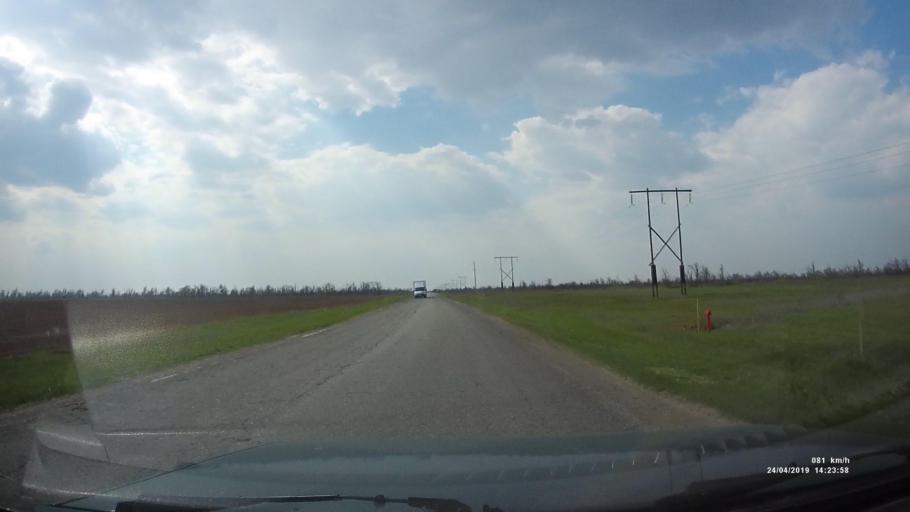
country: RU
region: Kalmykiya
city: Arshan'
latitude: 46.3255
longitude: 44.1081
